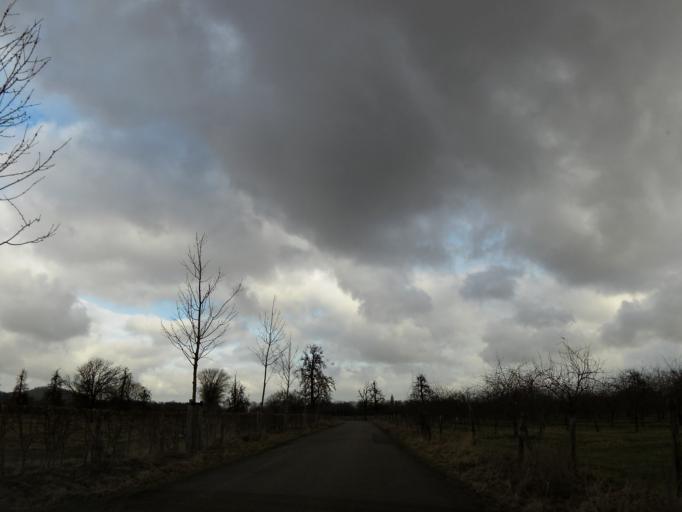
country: NL
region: Limburg
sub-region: Eijsden-Margraten
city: Eijsden
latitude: 50.7894
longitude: 5.7013
